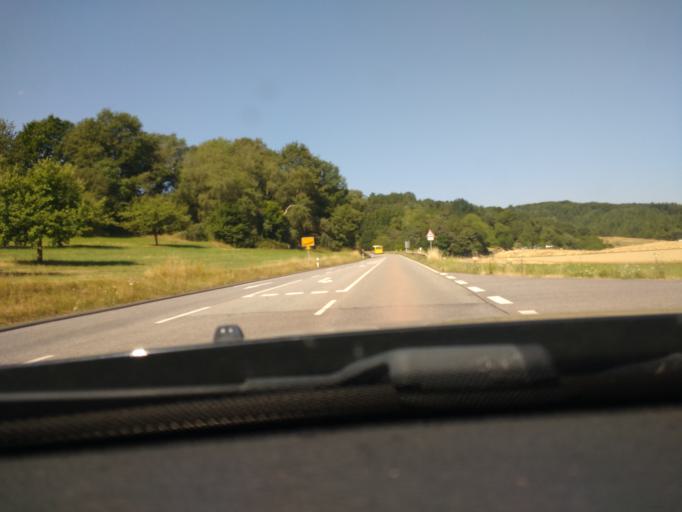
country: DE
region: Rheinland-Pfalz
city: Bausendorf
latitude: 50.0118
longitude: 6.9889
